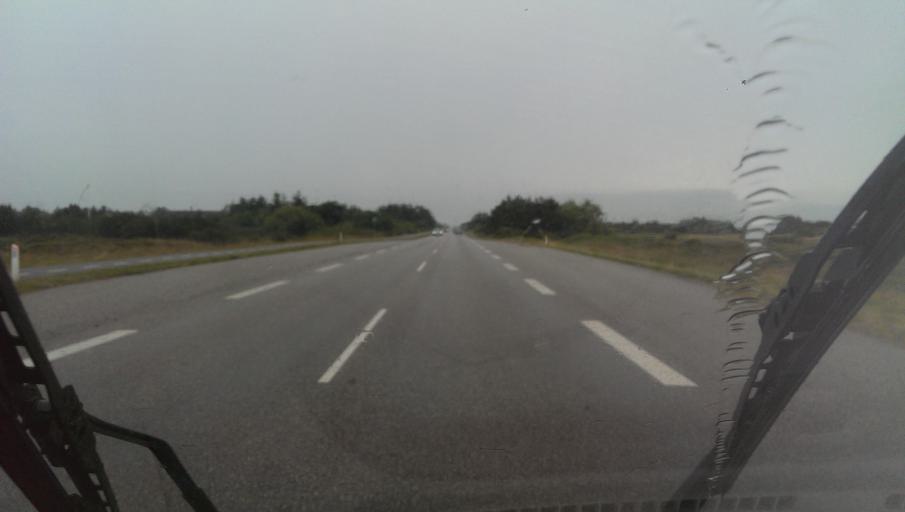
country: DK
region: Central Jutland
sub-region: Ringkobing-Skjern Kommune
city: Hvide Sande
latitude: 56.1043
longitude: 8.1268
